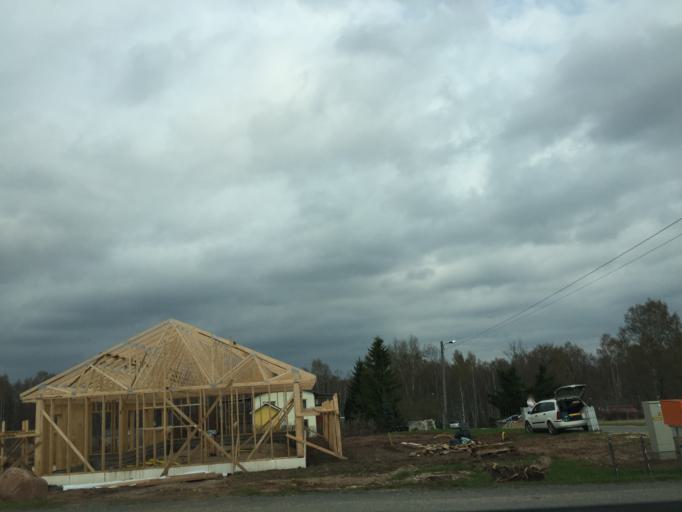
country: EE
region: Tartu
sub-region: Noo vald
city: Noo
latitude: 58.2713
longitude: 26.5422
